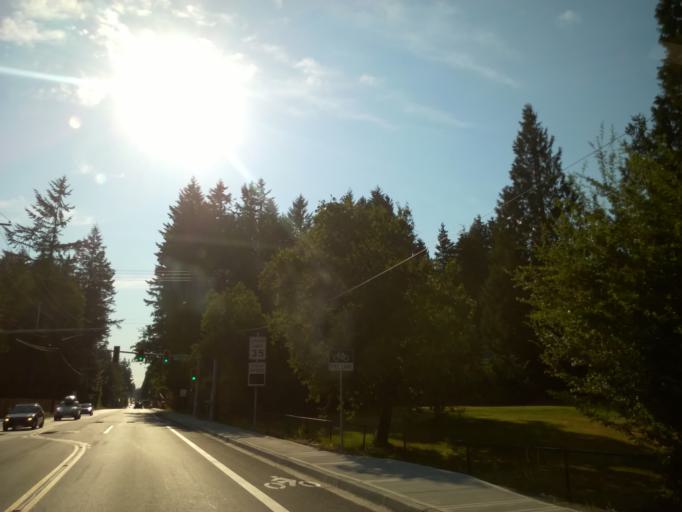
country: US
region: Washington
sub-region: King County
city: Cottage Lake
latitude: 47.7615
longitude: -122.1125
